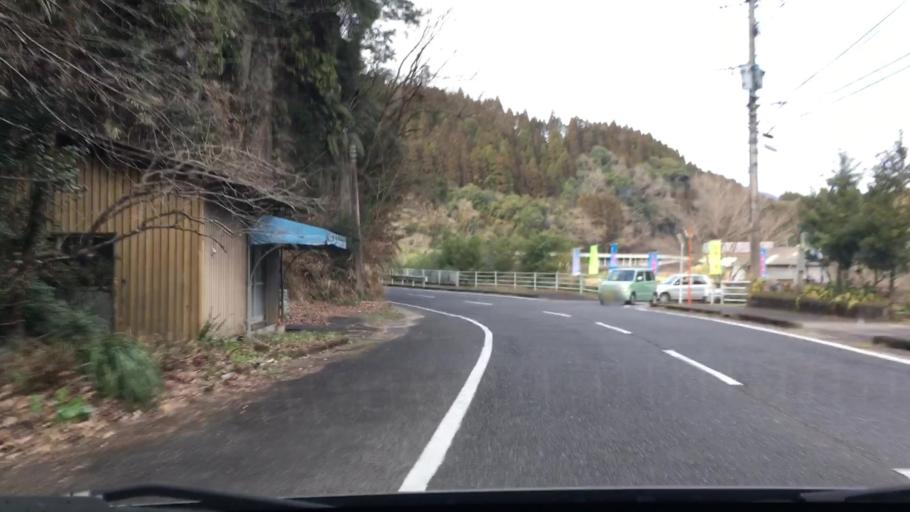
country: JP
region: Miyazaki
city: Kushima
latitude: 31.5452
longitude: 131.2423
